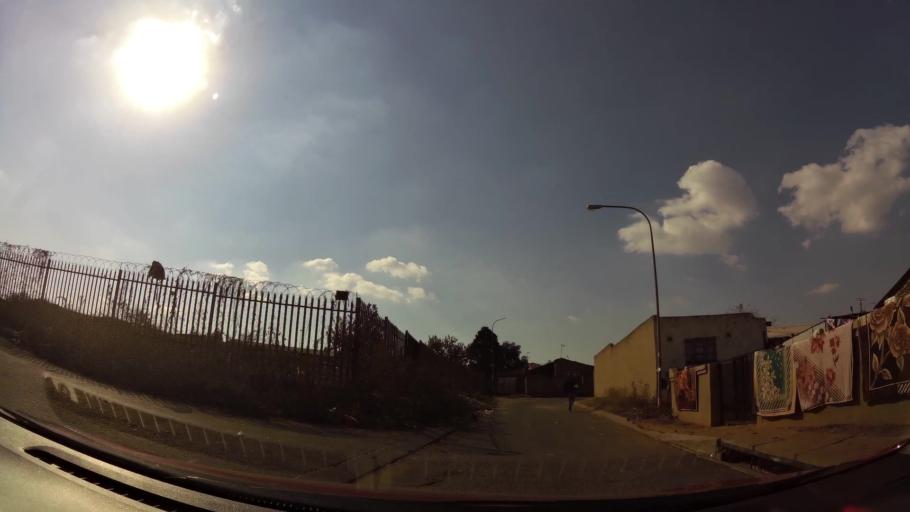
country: ZA
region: Gauteng
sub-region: City of Johannesburg Metropolitan Municipality
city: Soweto
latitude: -26.2522
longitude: 27.9429
